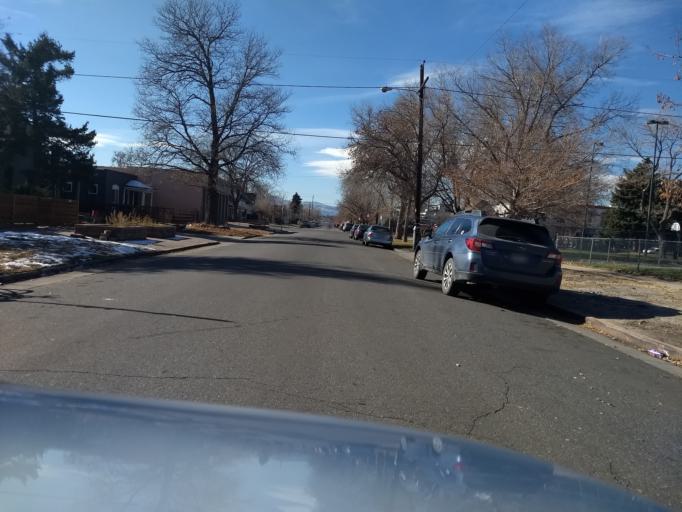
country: US
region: Colorado
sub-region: Denver County
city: Denver
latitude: 39.7226
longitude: -104.9954
